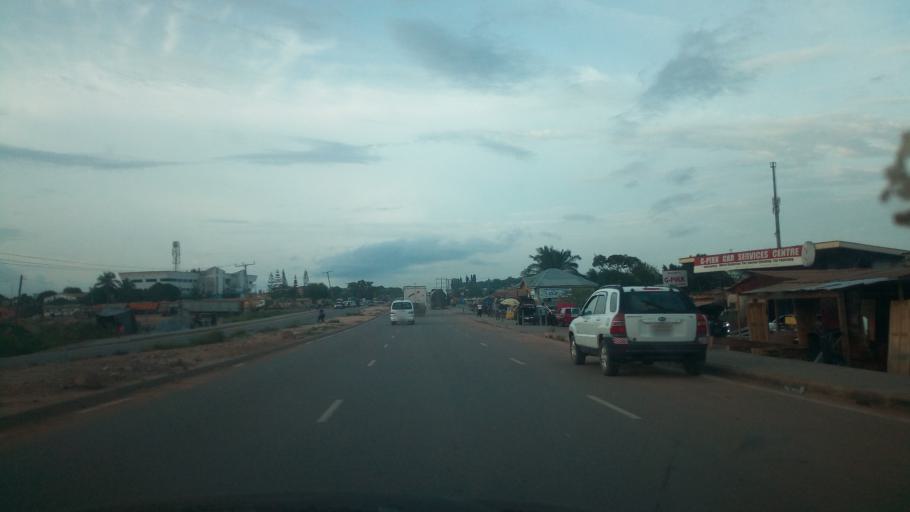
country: GH
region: Western
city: Takoradi
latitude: 4.9158
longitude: -1.7920
